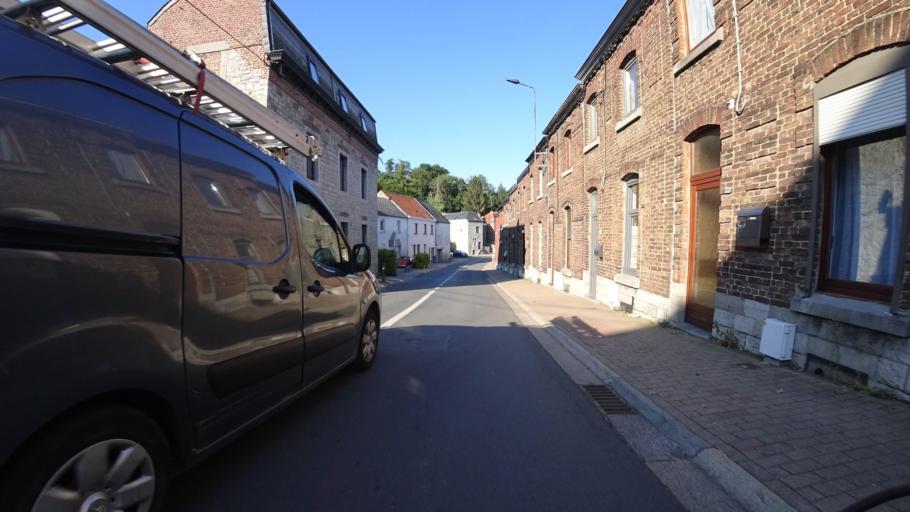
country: BE
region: Wallonia
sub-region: Province de Namur
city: Namur
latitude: 50.4692
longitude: 4.8354
